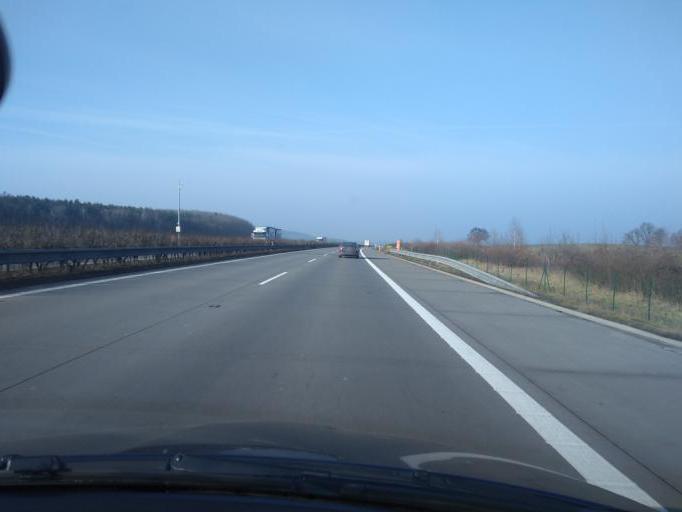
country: CZ
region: Central Bohemia
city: Zizelice
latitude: 50.1291
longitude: 15.3403
